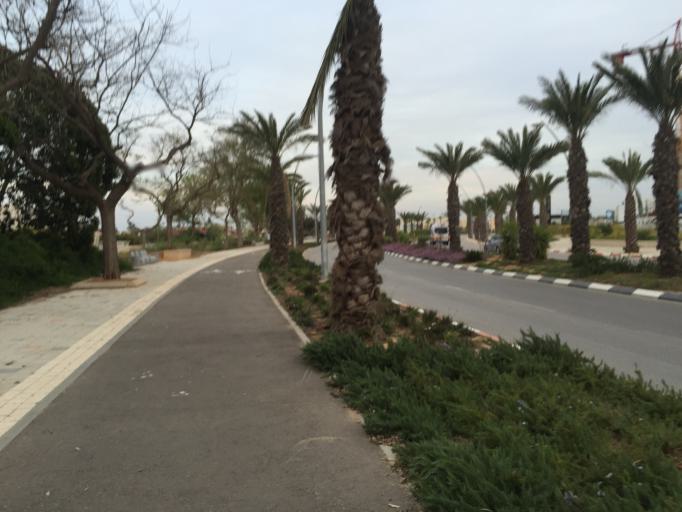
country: IL
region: Haifa
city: Qesarya
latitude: 32.5053
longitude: 34.9160
